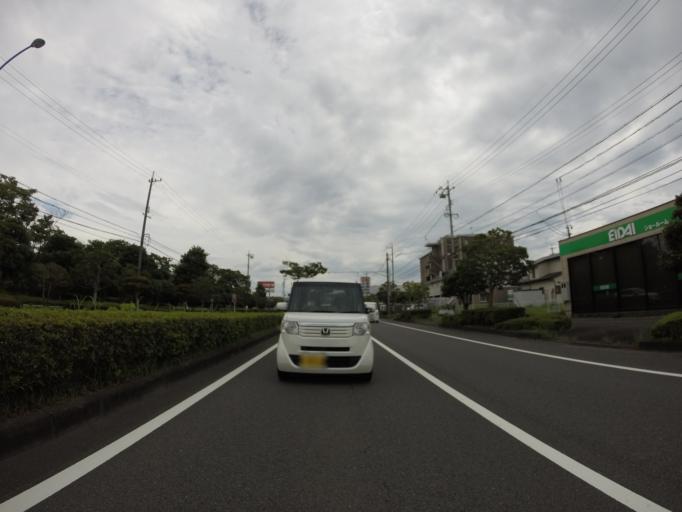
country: JP
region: Shizuoka
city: Shizuoka-shi
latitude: 34.9526
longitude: 138.4163
